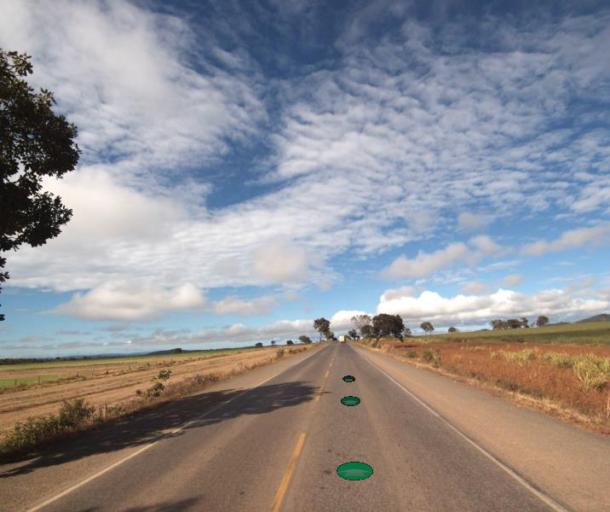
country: BR
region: Goias
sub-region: Uruacu
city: Uruacu
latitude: -14.6811
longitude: -49.2062
